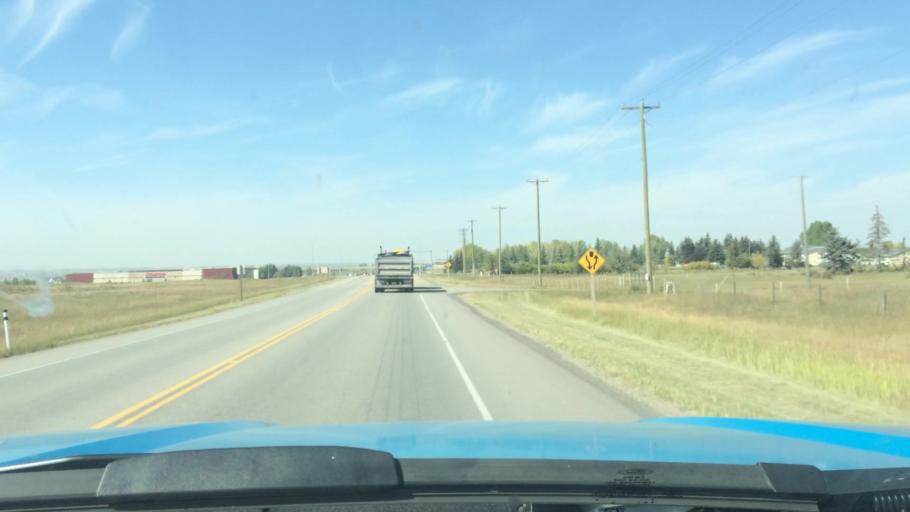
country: CA
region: Alberta
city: Airdrie
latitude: 51.2126
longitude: -113.9750
